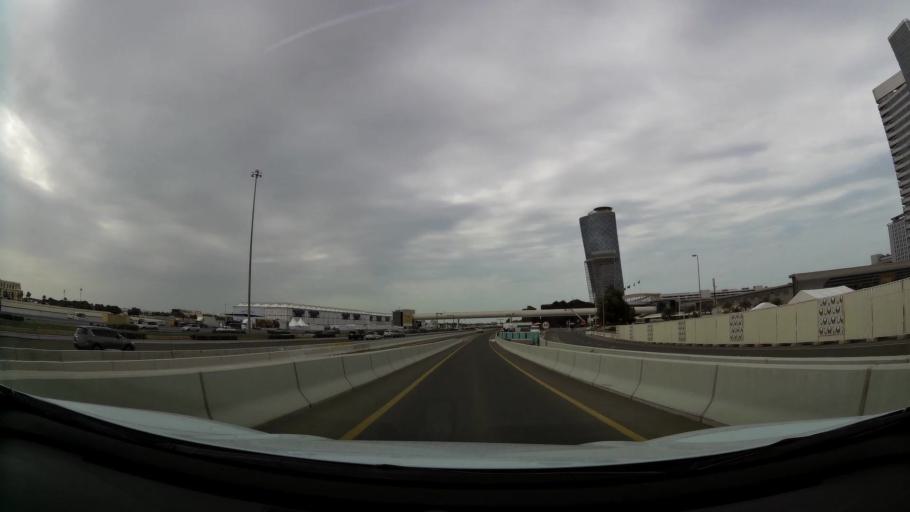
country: AE
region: Abu Dhabi
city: Abu Dhabi
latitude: 24.4165
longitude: 54.4404
